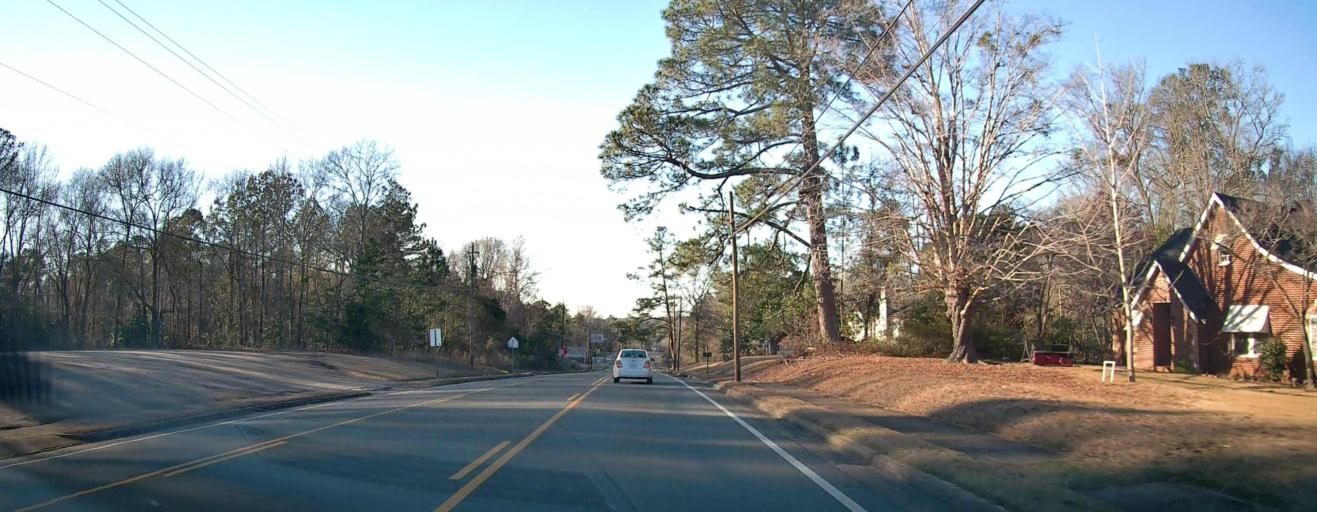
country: US
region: Georgia
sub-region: Meriwether County
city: Manchester
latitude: 32.8618
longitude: -84.6234
